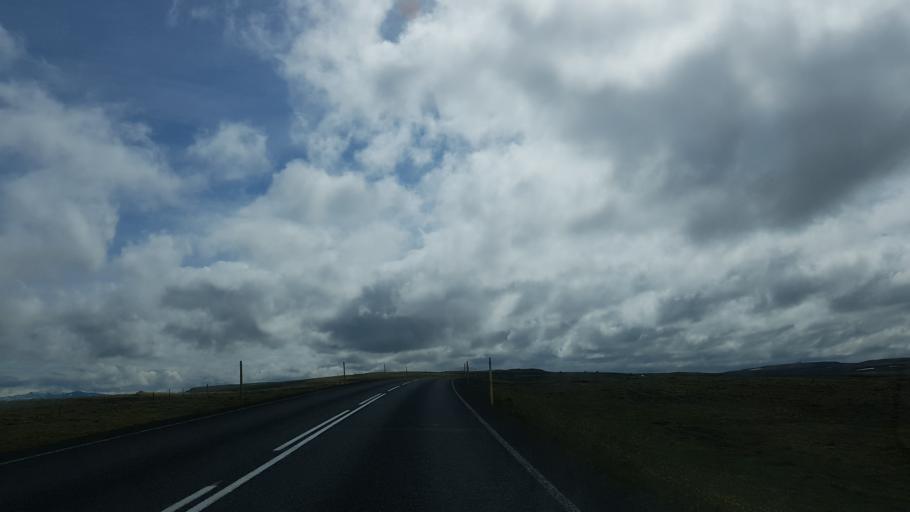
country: IS
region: West
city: Borgarnes
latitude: 65.0065
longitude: -21.0662
